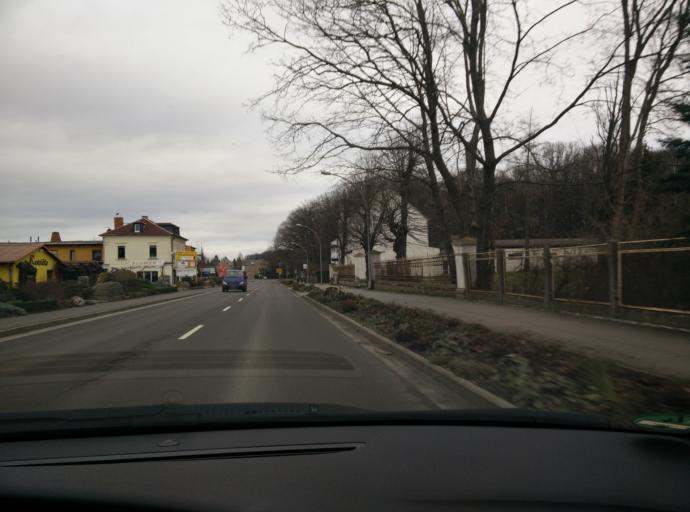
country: DE
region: Saxony
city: Frohburg
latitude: 51.0643
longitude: 12.5567
